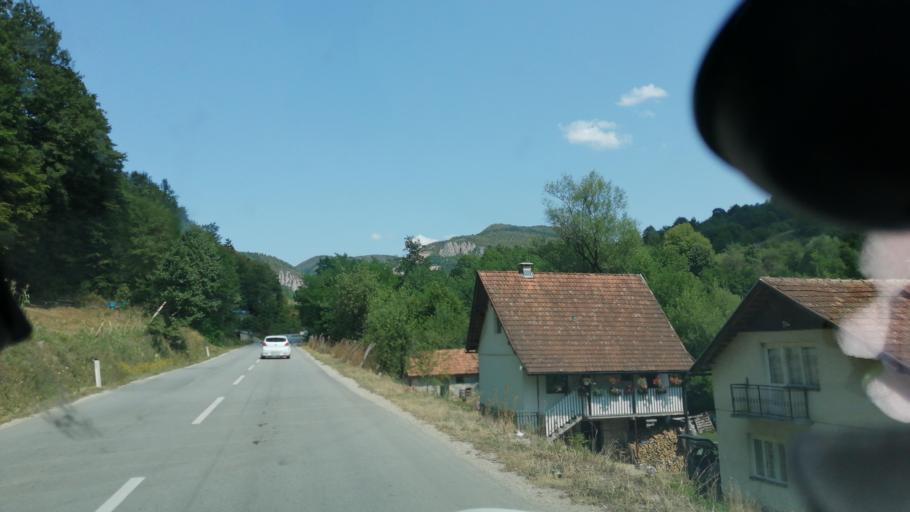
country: RS
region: Central Serbia
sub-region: Moravicki Okrug
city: Ivanjica
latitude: 43.6097
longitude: 20.2353
